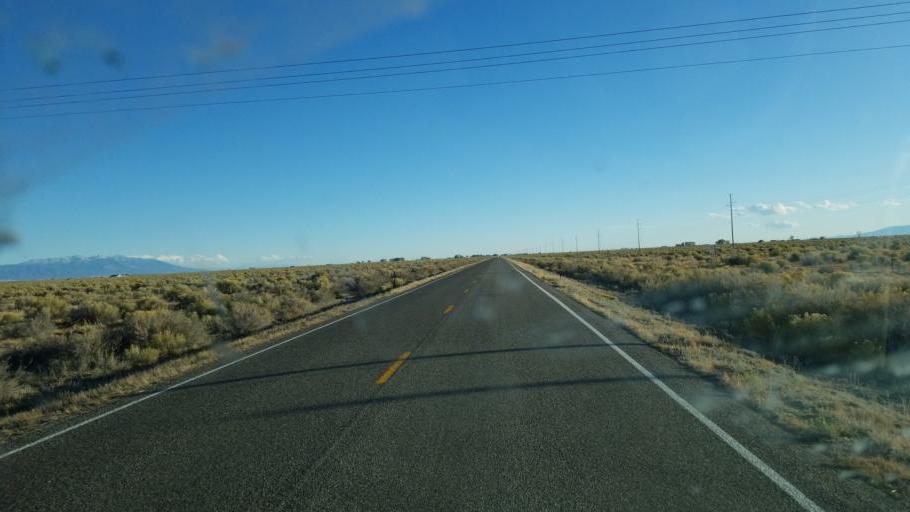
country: US
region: Colorado
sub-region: Saguache County
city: Saguache
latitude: 38.0713
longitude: -105.9166
